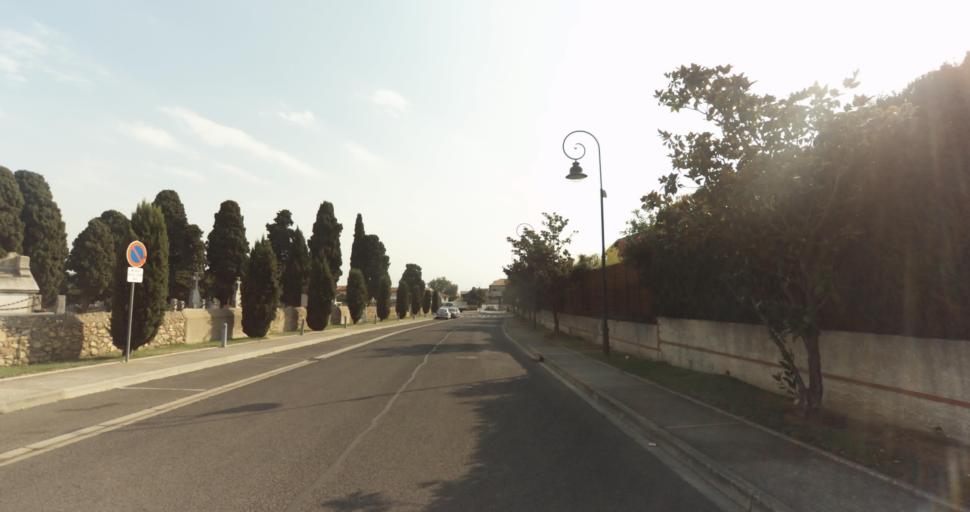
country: FR
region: Languedoc-Roussillon
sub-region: Departement des Pyrenees-Orientales
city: Latour-Bas-Elne
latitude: 42.6160
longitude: 2.9980
